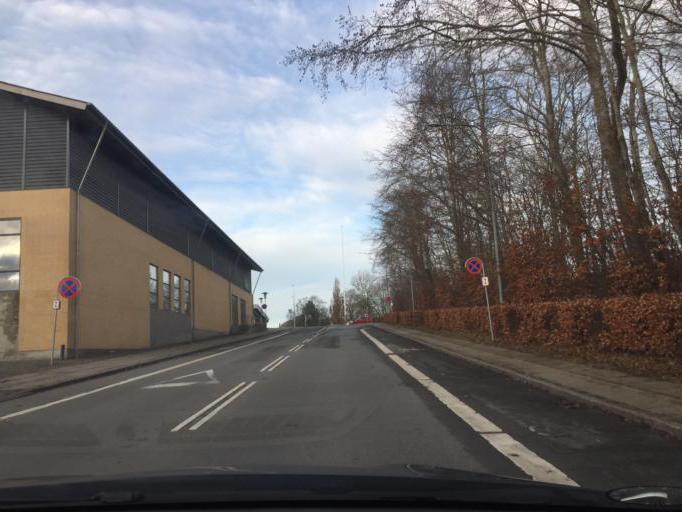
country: DK
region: South Denmark
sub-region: Faaborg-Midtfyn Kommune
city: Ringe
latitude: 55.2402
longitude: 10.4745
